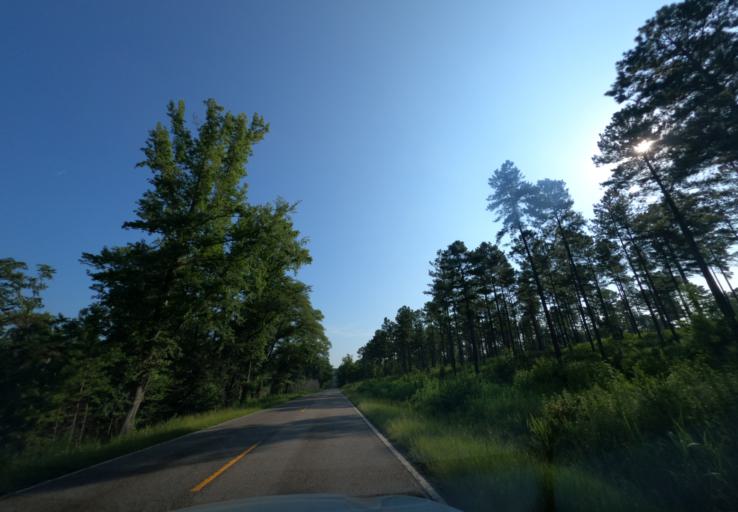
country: US
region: South Carolina
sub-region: Edgefield County
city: Edgefield
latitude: 33.7489
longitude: -81.9589
